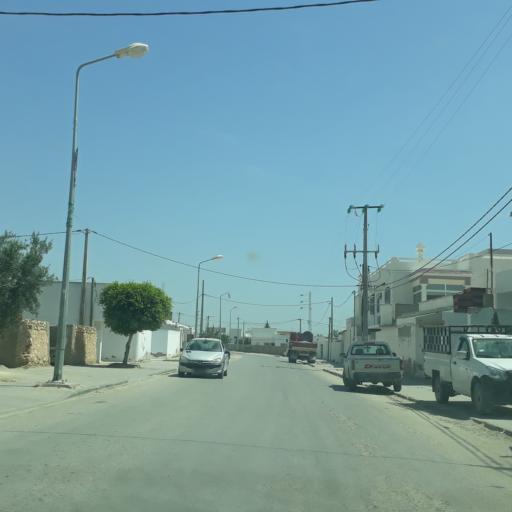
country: TN
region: Safaqis
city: Al Qarmadah
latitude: 34.8181
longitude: 10.7759
